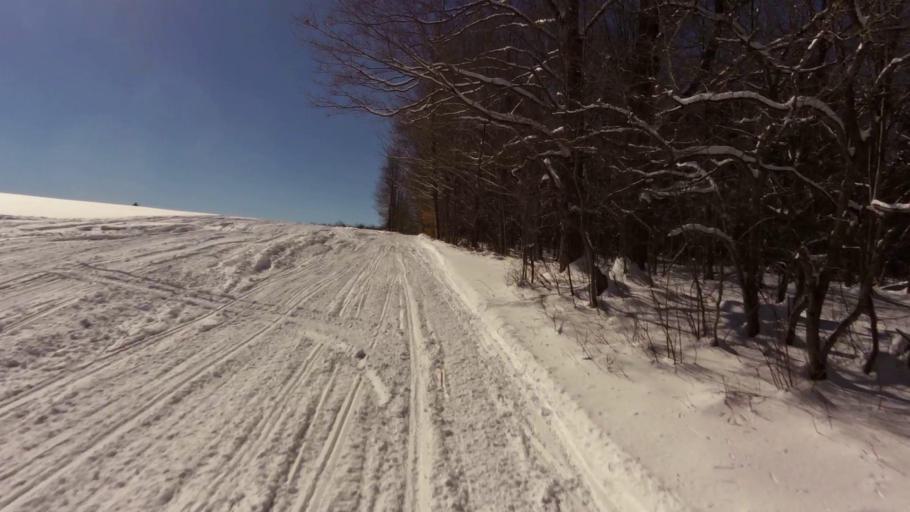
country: US
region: New York
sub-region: Chautauqua County
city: Mayville
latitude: 42.2370
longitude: -79.5184
